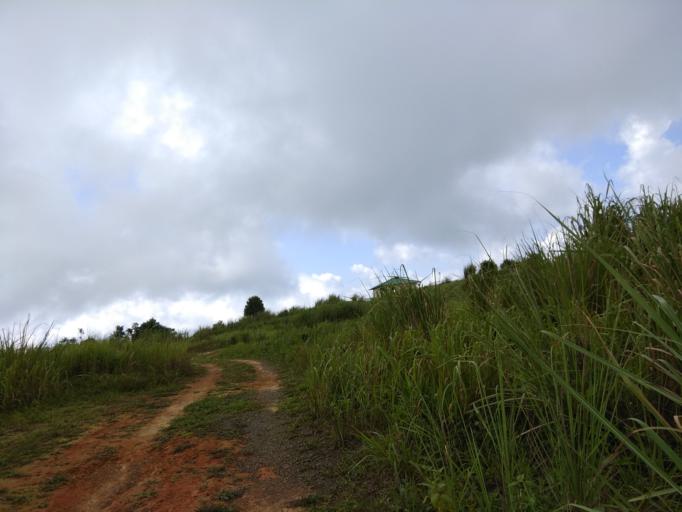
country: BD
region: Chittagong
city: Bandarban
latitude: 21.7435
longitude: 92.4181
